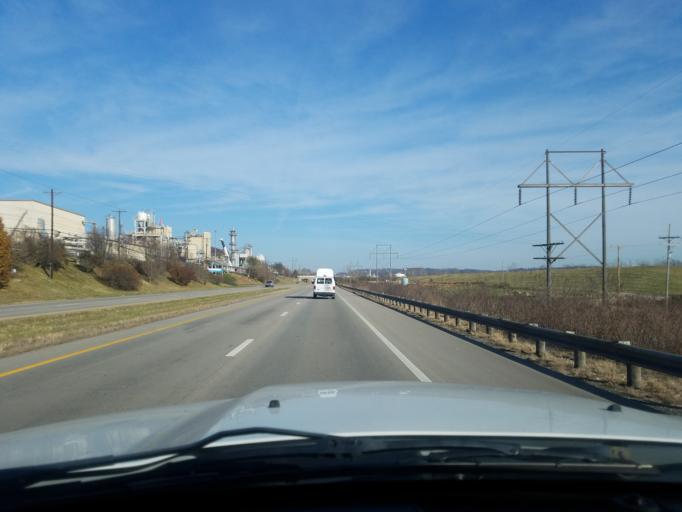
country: US
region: West Virginia
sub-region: Wood County
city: Boaz
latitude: 39.3695
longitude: -81.5173
